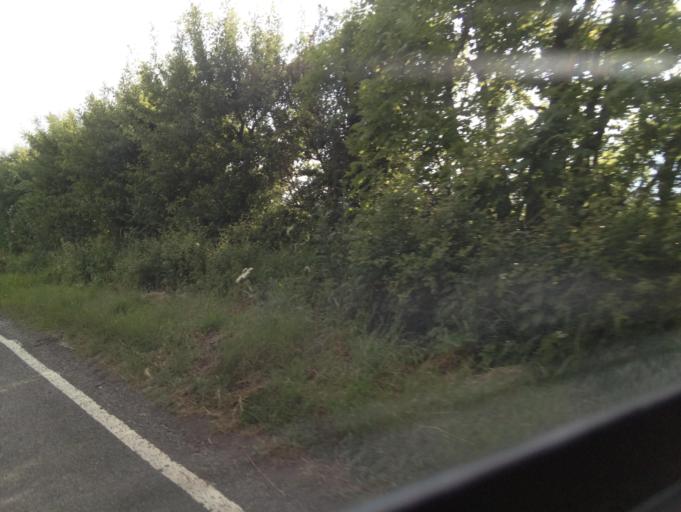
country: GB
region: England
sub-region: Lincolnshire
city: Great Gonerby
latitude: 52.9704
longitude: -0.6871
